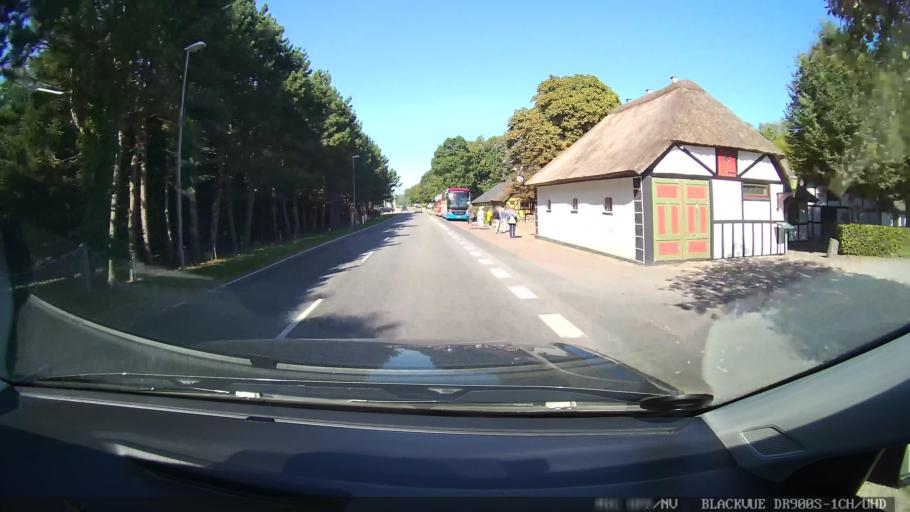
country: DK
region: Central Jutland
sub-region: Randers Kommune
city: Spentrup
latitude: 56.5539
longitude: 10.0017
